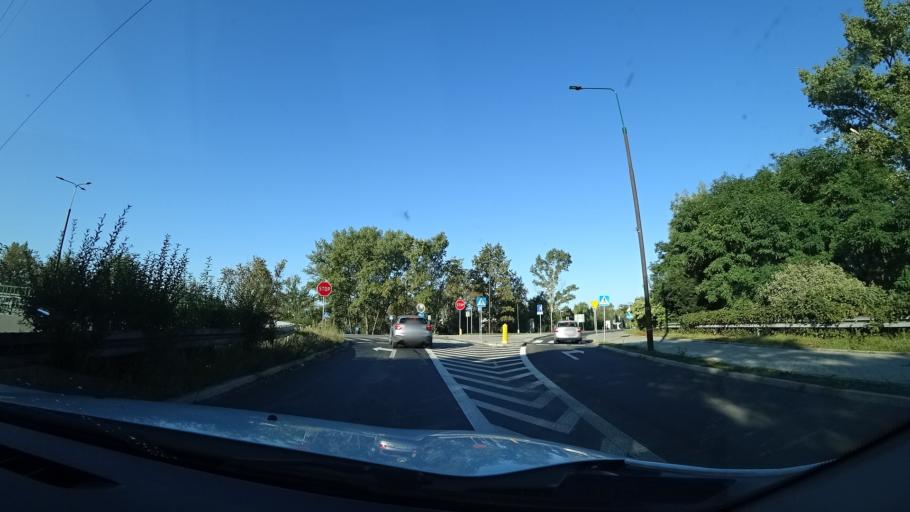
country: PL
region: Silesian Voivodeship
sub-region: Powiat bedzinski
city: Bedzin
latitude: 50.2947
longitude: 19.1680
